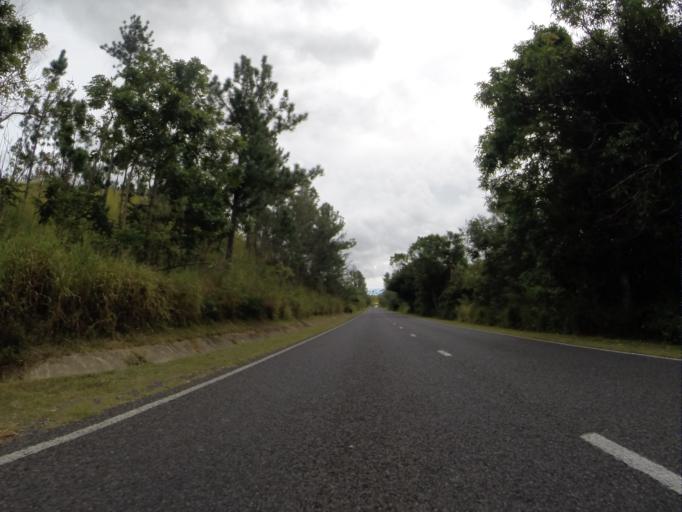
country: FJ
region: Western
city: Nadi
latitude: -17.9996
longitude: 177.3195
